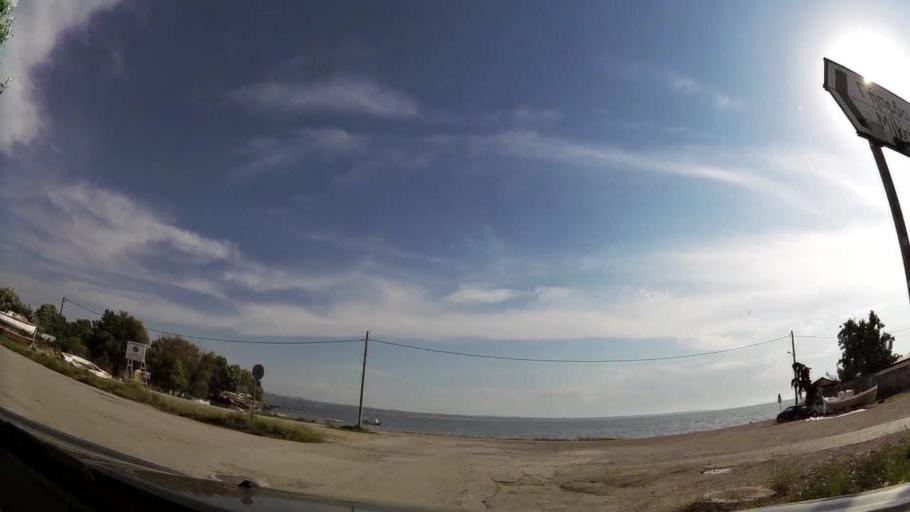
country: GR
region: Central Macedonia
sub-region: Nomos Thessalonikis
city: Kalamaria
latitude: 40.5650
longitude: 22.9610
